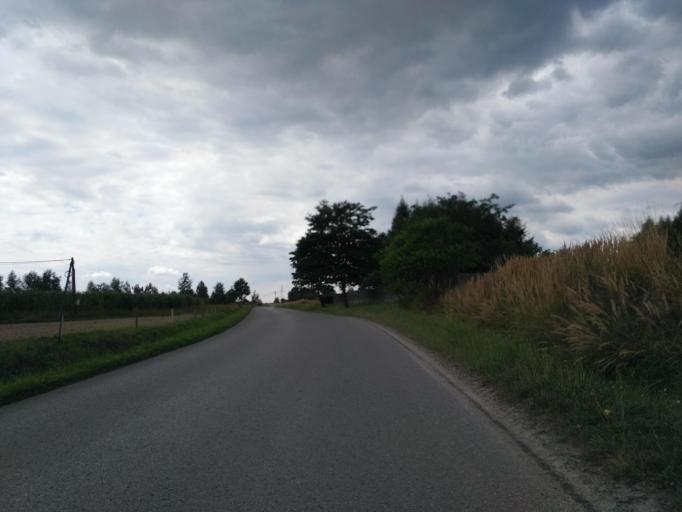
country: PL
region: Subcarpathian Voivodeship
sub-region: Powiat rzeszowski
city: Tyczyn
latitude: 49.9333
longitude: 22.0399
